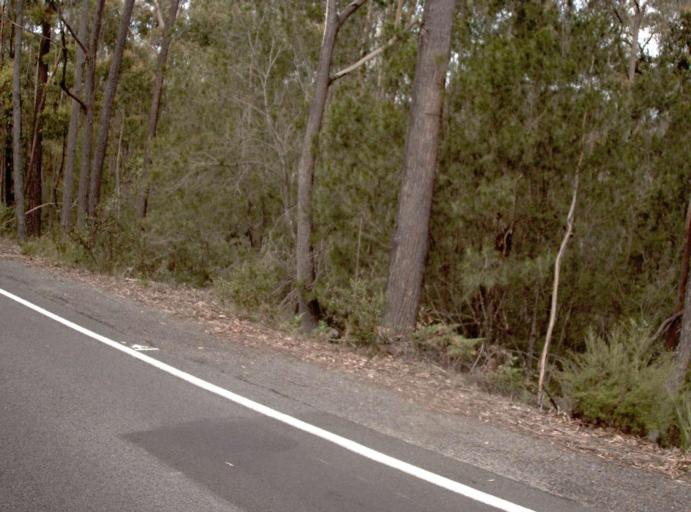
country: AU
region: New South Wales
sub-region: Bega Valley
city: Eden
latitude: -37.4942
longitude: 149.5492
